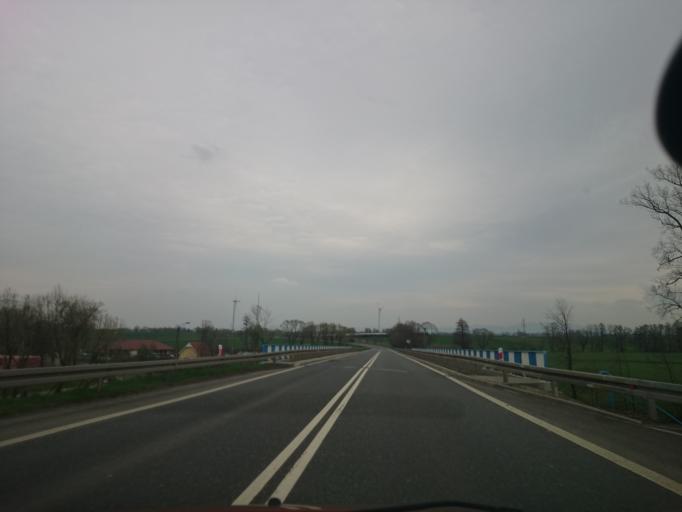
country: PL
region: Opole Voivodeship
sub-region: Powiat nyski
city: Paczkow
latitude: 50.4571
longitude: 16.9839
